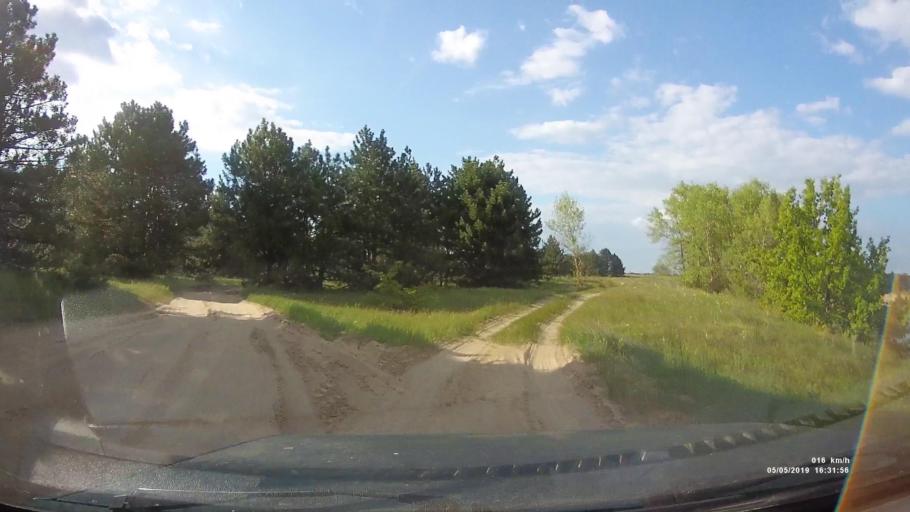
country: RU
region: Rostov
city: Ust'-Donetskiy
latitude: 47.7776
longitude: 41.0142
